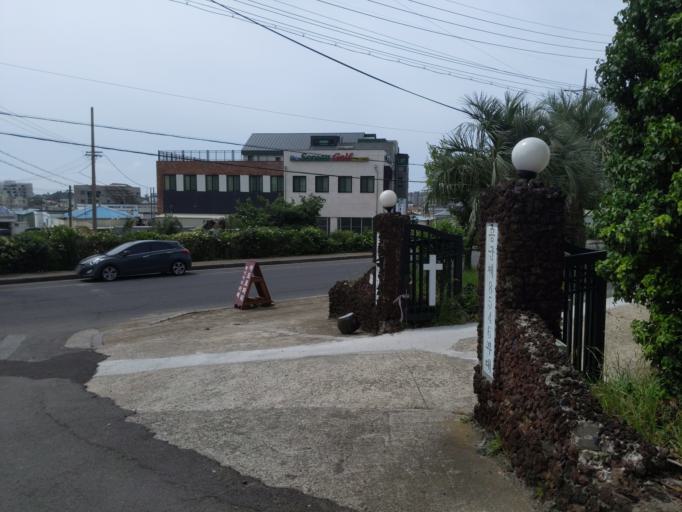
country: KR
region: Jeju-do
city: Gaigeturi
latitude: 33.2267
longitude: 126.2581
